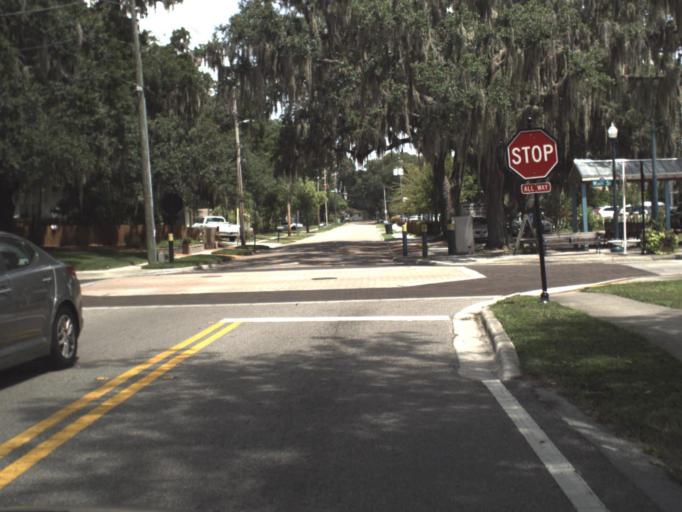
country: US
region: Florida
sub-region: Pinellas County
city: Safety Harbor
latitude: 27.9906
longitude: -82.6980
